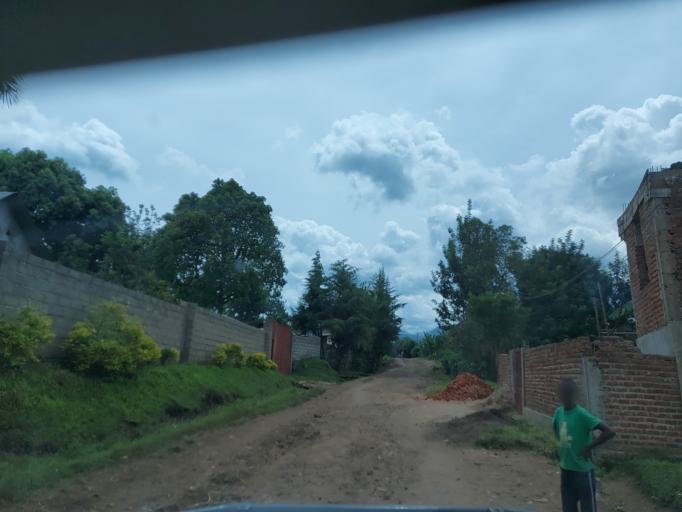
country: CD
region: South Kivu
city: Bukavu
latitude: -2.2440
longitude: 28.8167
